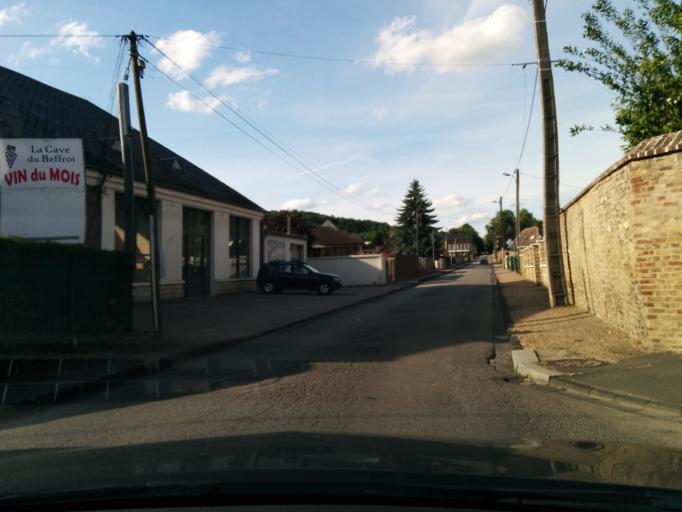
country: FR
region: Haute-Normandie
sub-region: Departement de l'Eure
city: Les Andelys
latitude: 49.2490
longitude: 1.4135
